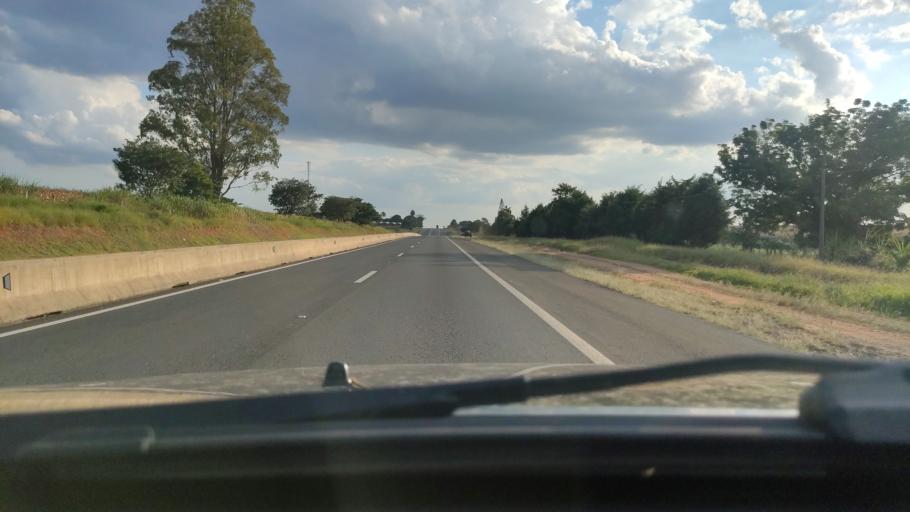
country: BR
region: Sao Paulo
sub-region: Artur Nogueira
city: Artur Nogueira
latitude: -22.4616
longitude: -47.1017
